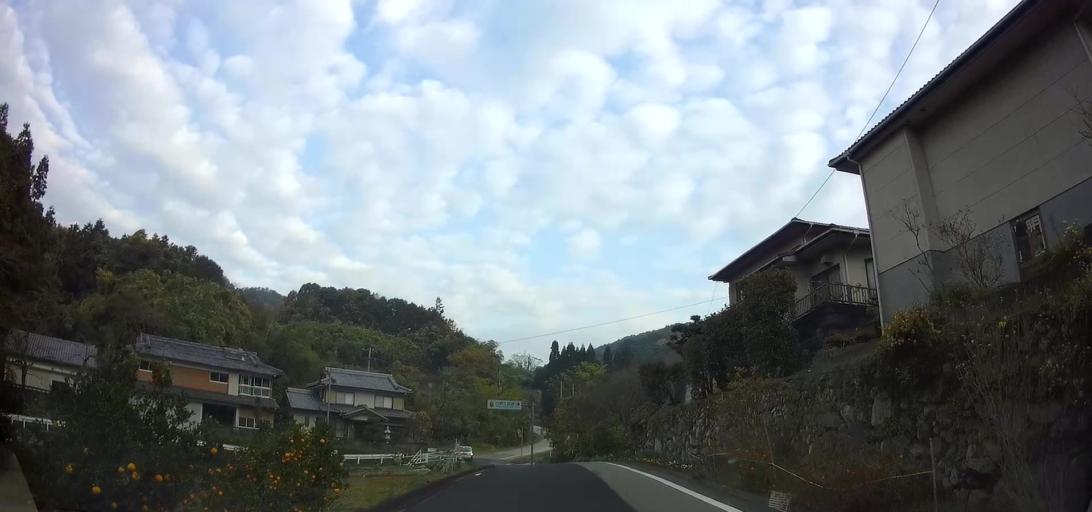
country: JP
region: Nagasaki
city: Shimabara
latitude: 32.6591
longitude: 130.2494
